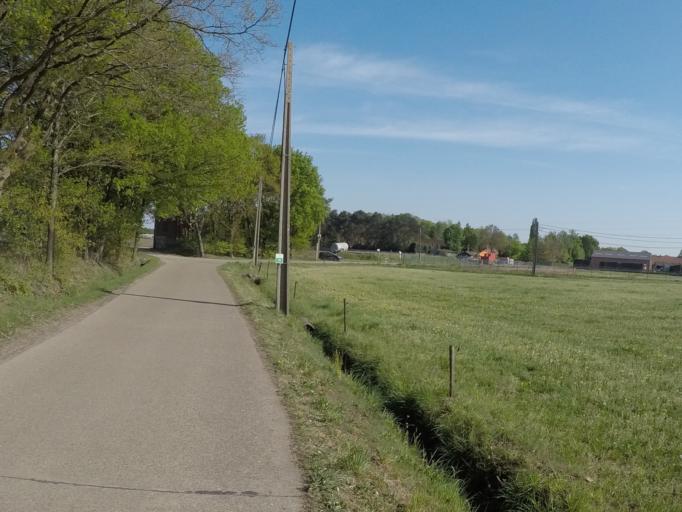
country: BE
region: Flanders
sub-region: Provincie Antwerpen
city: Nijlen
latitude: 51.1534
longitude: 4.7014
